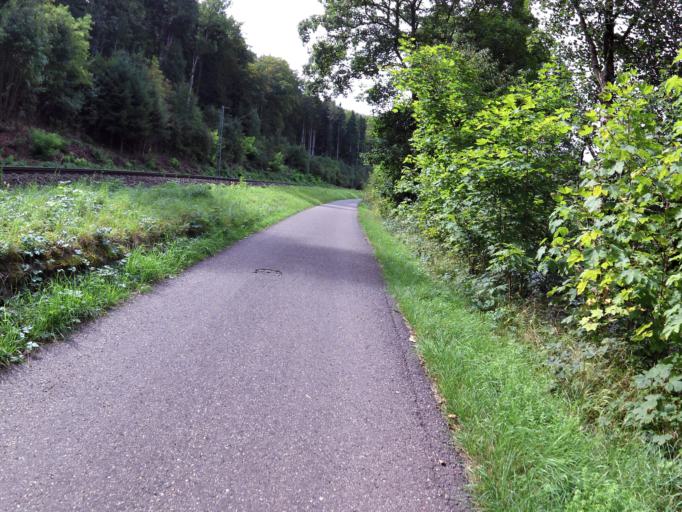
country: DE
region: Baden-Wuerttemberg
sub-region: Karlsruhe Region
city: Horb am Neckar
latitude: 48.4272
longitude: 8.6611
